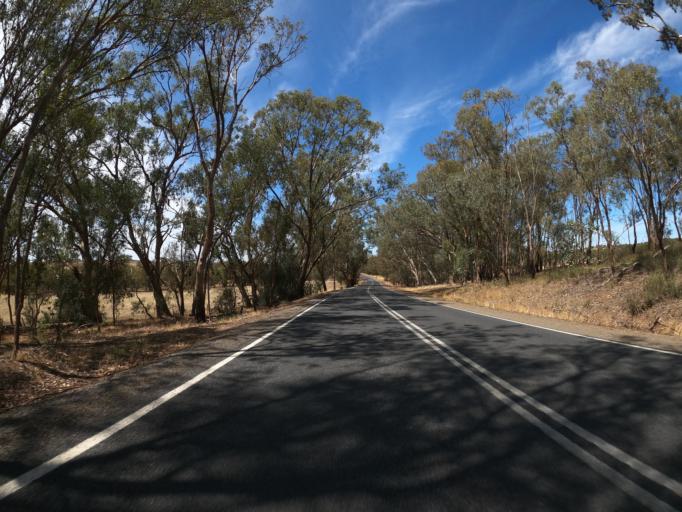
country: AU
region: Victoria
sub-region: Benalla
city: Benalla
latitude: -36.3895
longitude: 145.9800
